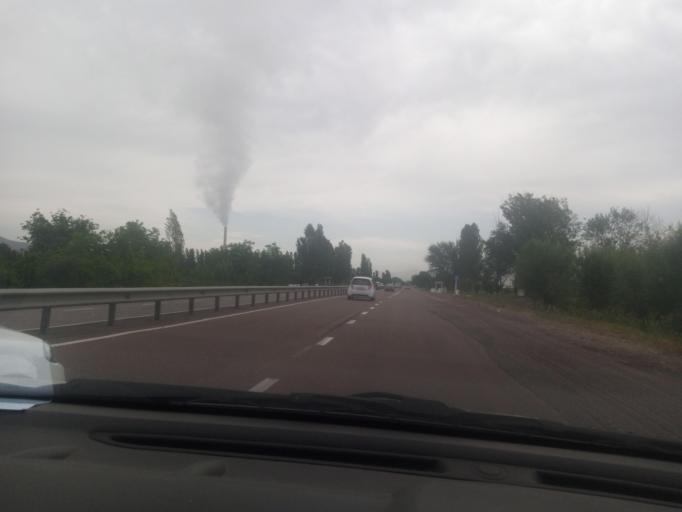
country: UZ
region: Toshkent
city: Ohangaron
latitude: 40.9085
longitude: 69.7774
